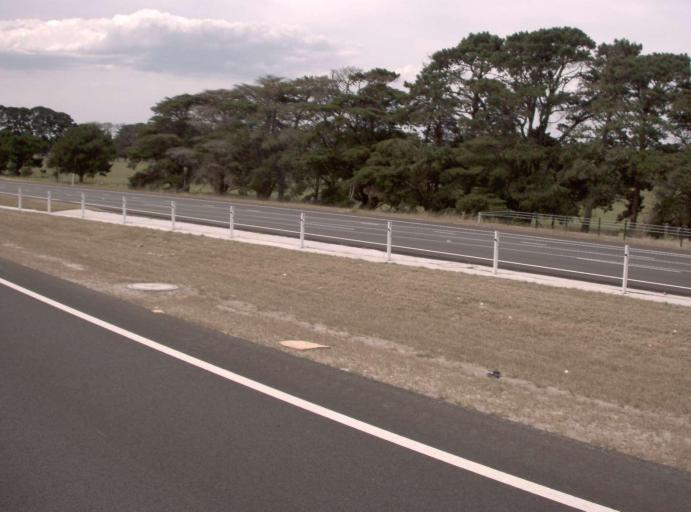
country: AU
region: Victoria
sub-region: Mornington Peninsula
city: Moorooduc
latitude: -38.2379
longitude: 145.1238
